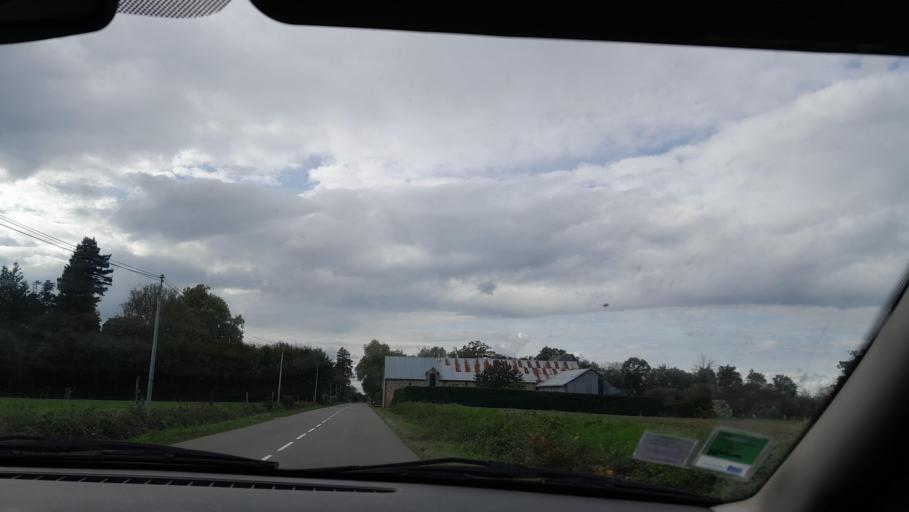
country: FR
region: Brittany
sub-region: Departement d'Ille-et-Vilaine
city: Argentre-du-Plessis
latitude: 48.0512
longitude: -1.0981
